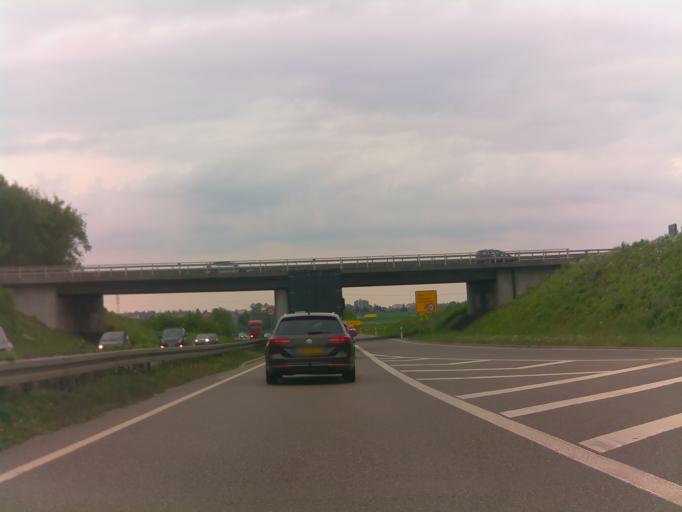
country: DE
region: Baden-Wuerttemberg
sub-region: Regierungsbezirk Stuttgart
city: Magstadt
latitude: 48.6999
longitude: 8.9663
